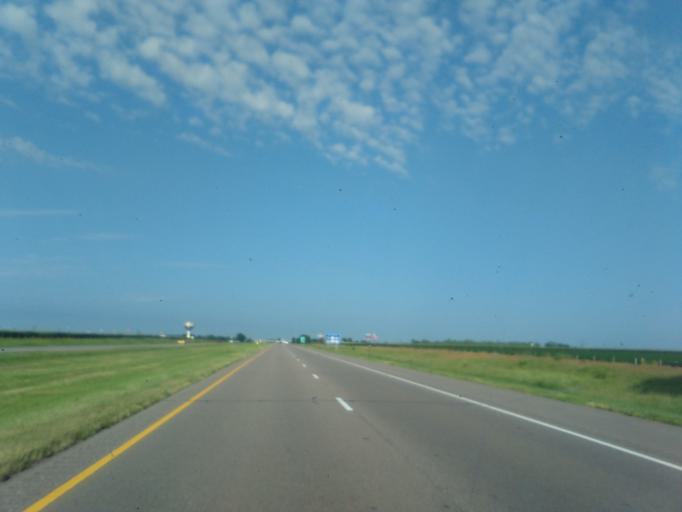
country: US
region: Nebraska
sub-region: York County
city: York
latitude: 40.8212
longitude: -97.6150
